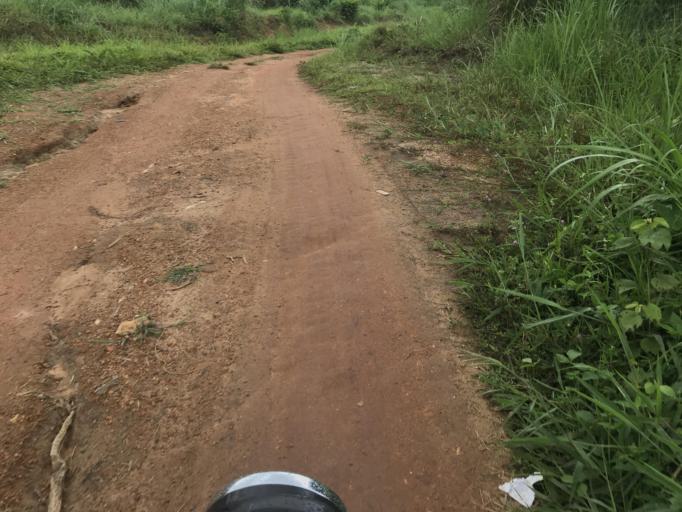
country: GN
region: Nzerekore
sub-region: Prefecture de Guekedou
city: Gueckedou
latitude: 8.4734
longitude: -10.2857
